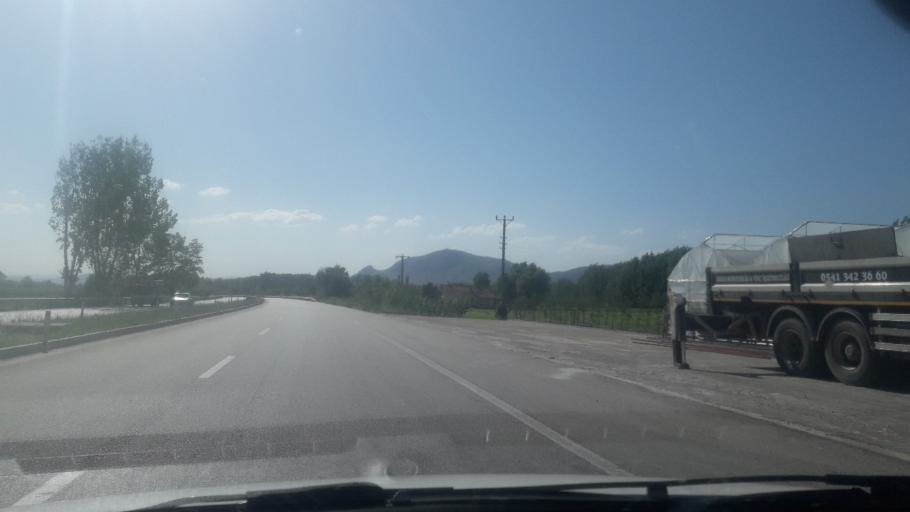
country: TR
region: Tokat
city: Dokmetepe
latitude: 40.3127
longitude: 36.2807
